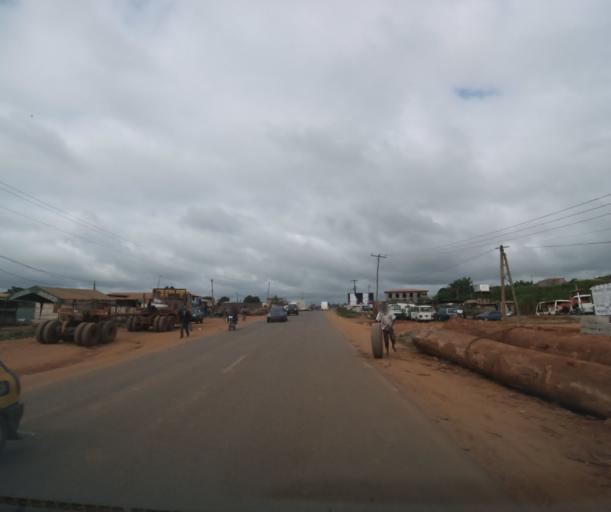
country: CM
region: Centre
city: Yaounde
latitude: 3.8018
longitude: 11.5066
